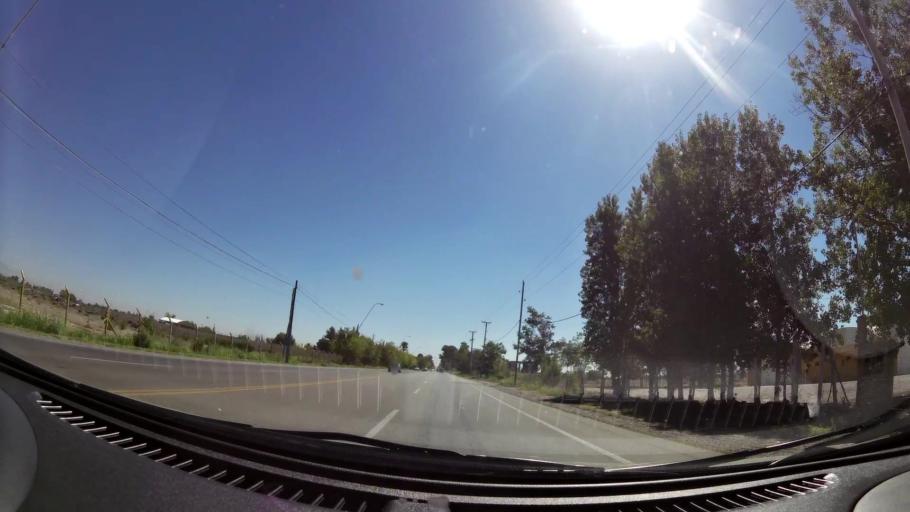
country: AR
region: San Juan
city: Villa Aberastain
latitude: -31.6211
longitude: -68.5505
